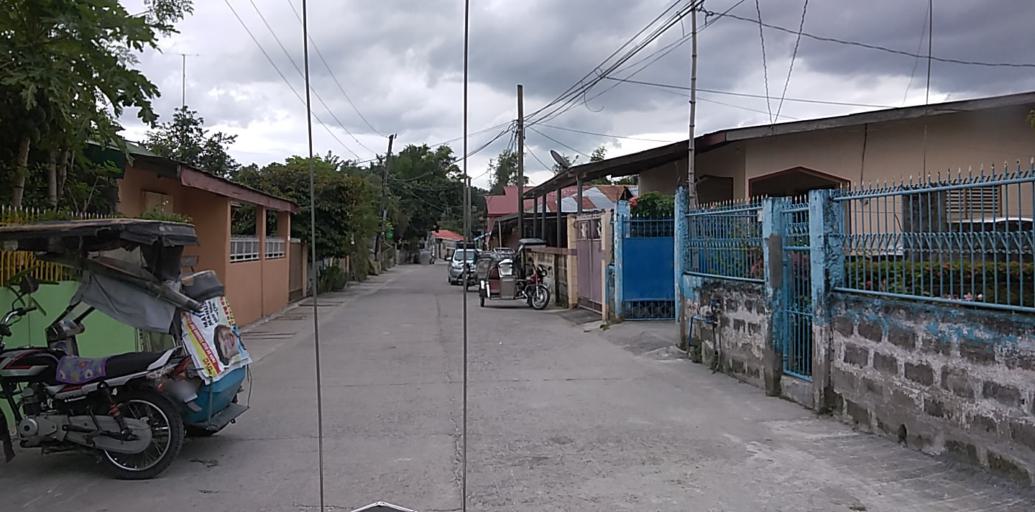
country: PH
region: Central Luzon
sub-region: Province of Pampanga
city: Porac
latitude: 15.0653
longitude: 120.5336
